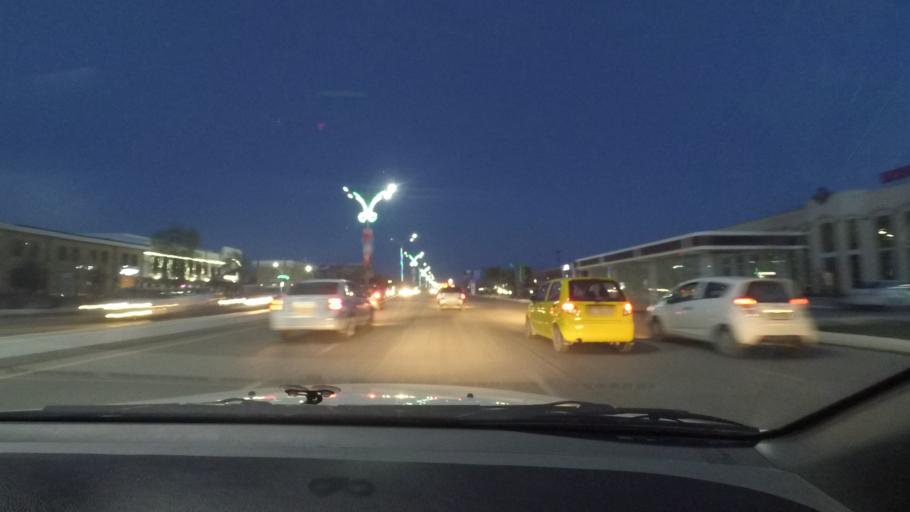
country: UZ
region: Bukhara
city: Bukhara
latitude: 39.7836
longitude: 64.4159
